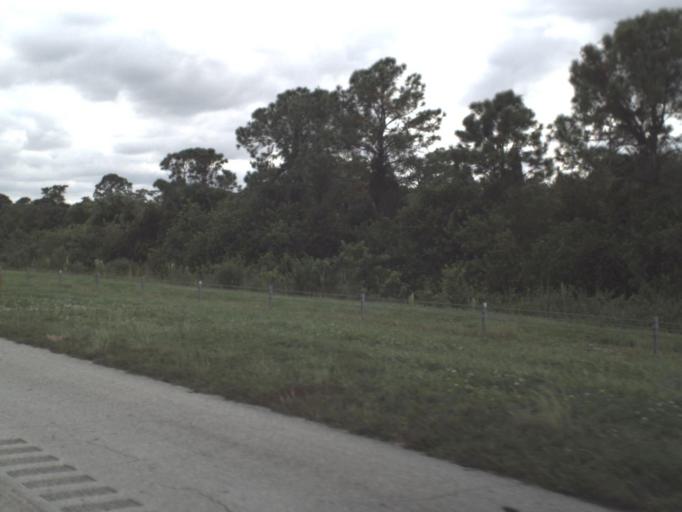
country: US
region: Florida
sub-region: Palm Beach County
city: Limestone Creek
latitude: 26.9063
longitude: -80.1414
